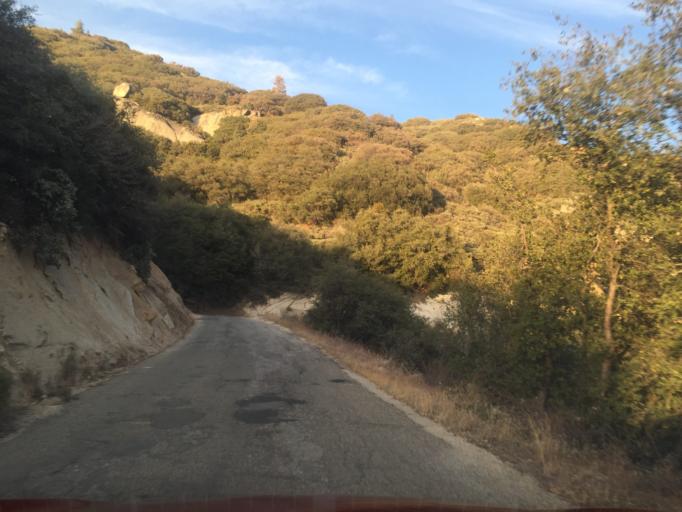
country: US
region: California
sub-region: Tulare County
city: Three Rivers
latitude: 36.4364
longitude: -118.7293
